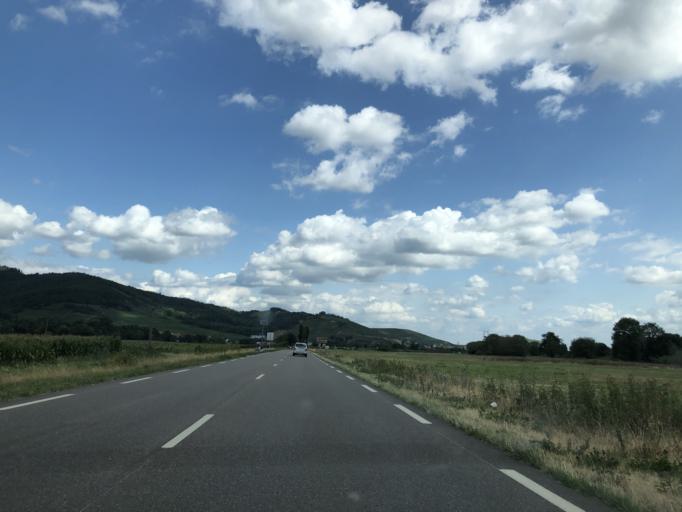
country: FR
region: Alsace
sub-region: Departement du Haut-Rhin
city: Turckheim
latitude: 48.0722
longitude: 7.2541
